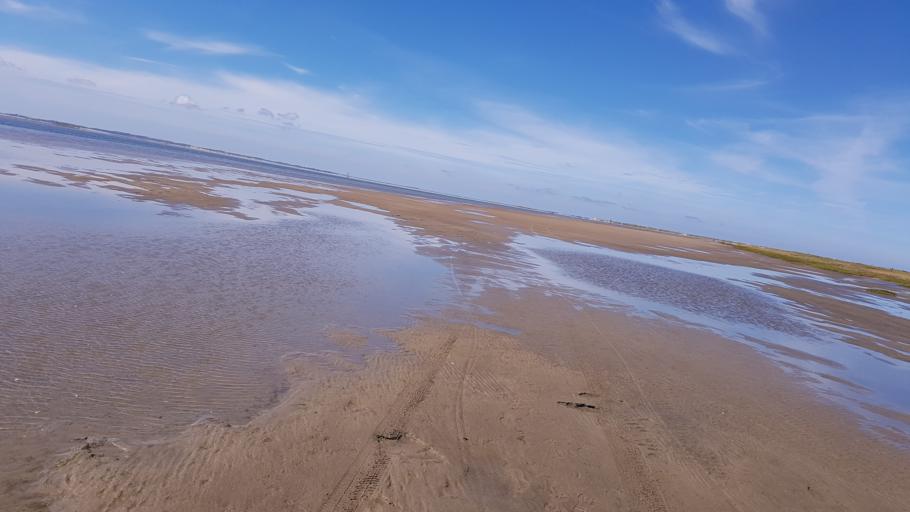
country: DE
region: Schleswig-Holstein
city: List
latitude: 55.0746
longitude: 8.5426
